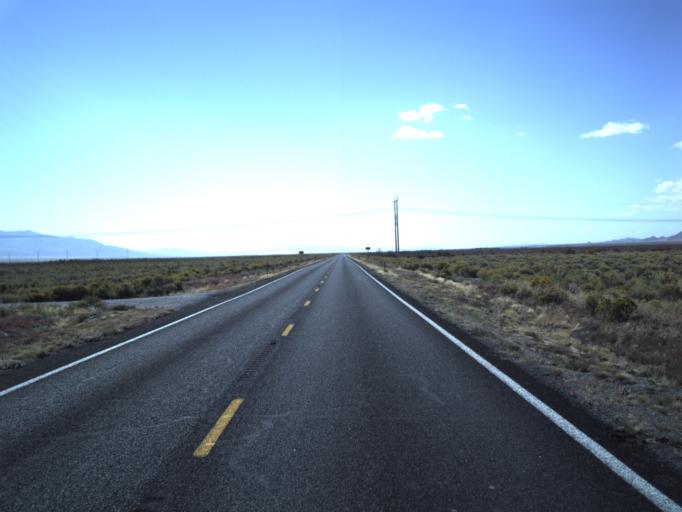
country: US
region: Utah
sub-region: Beaver County
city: Milford
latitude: 38.5766
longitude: -112.9895
